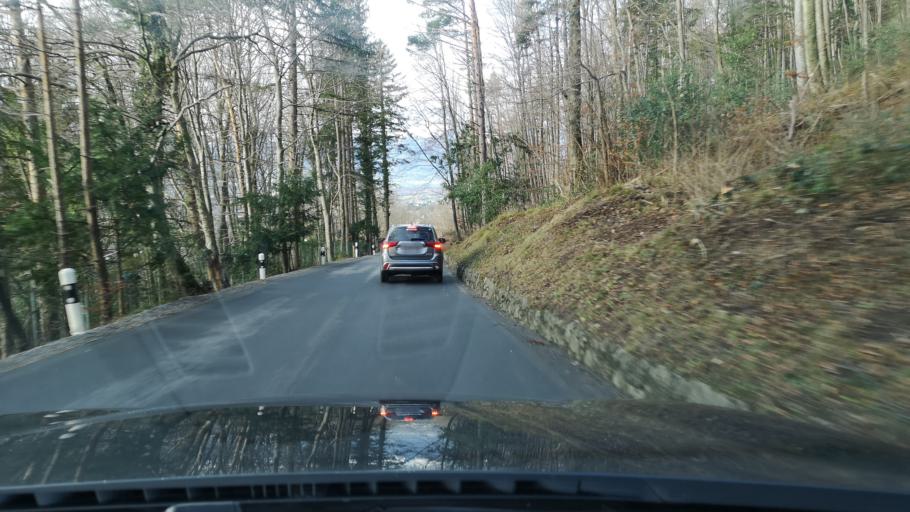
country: LI
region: Vaduz
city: Vaduz
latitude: 47.1368
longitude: 9.5271
